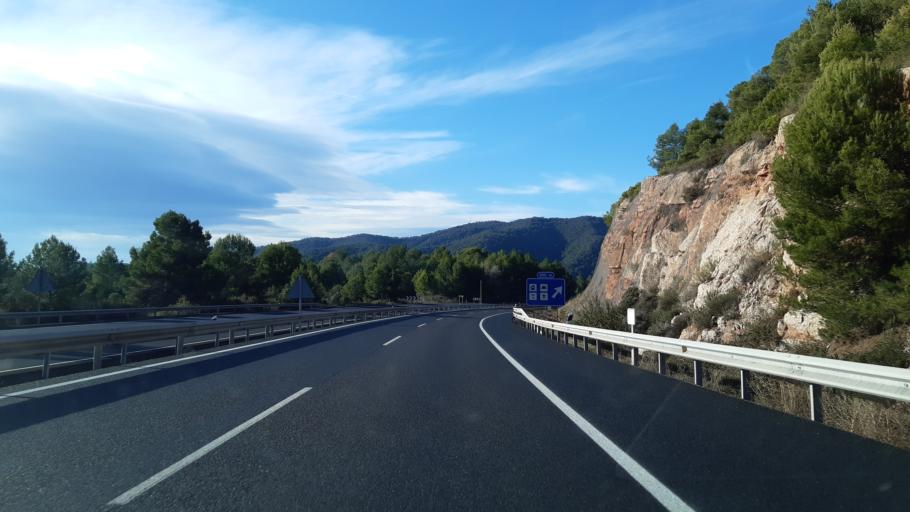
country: ES
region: Catalonia
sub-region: Provincia de Barcelona
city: Castelloli
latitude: 41.5933
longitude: 1.7601
